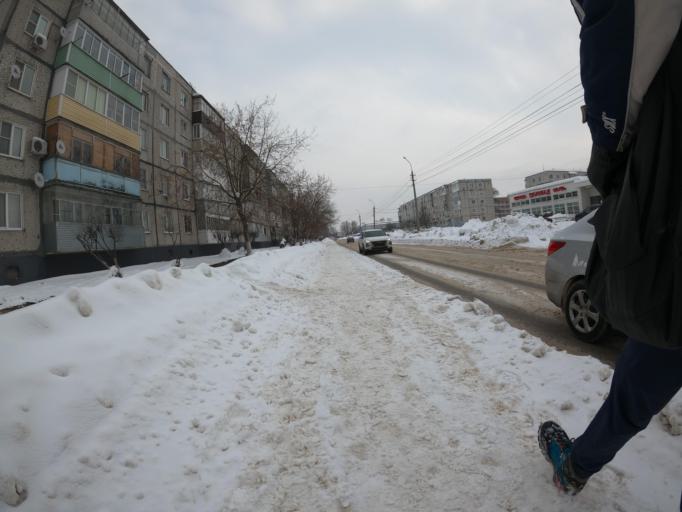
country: RU
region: Moskovskaya
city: Elektrogorsk
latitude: 55.8837
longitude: 38.7782
